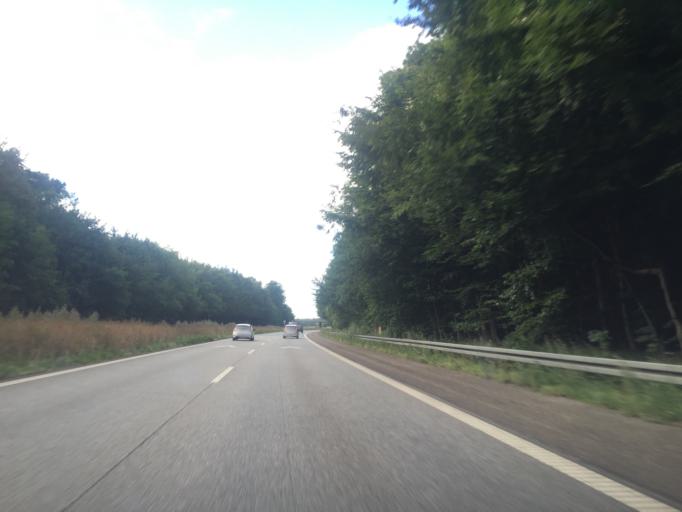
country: DK
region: Zealand
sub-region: Koge Kommune
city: Ejby
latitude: 55.4148
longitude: 12.1014
